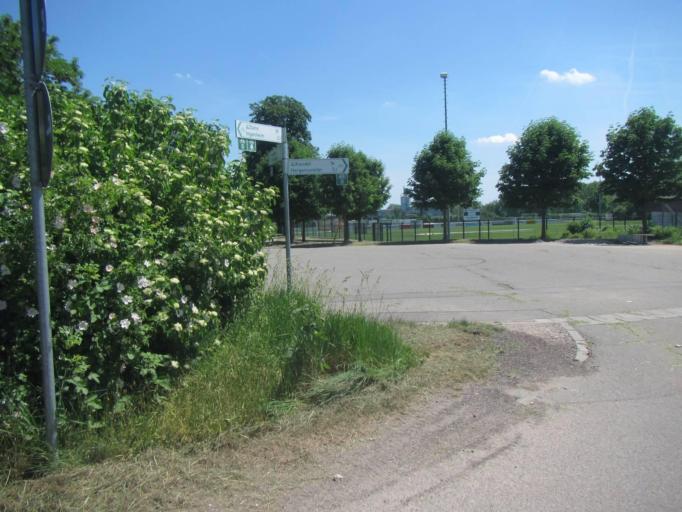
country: DE
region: Rheinland-Pfalz
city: Billigheim-Ingenheim
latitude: 49.1341
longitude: 8.1094
